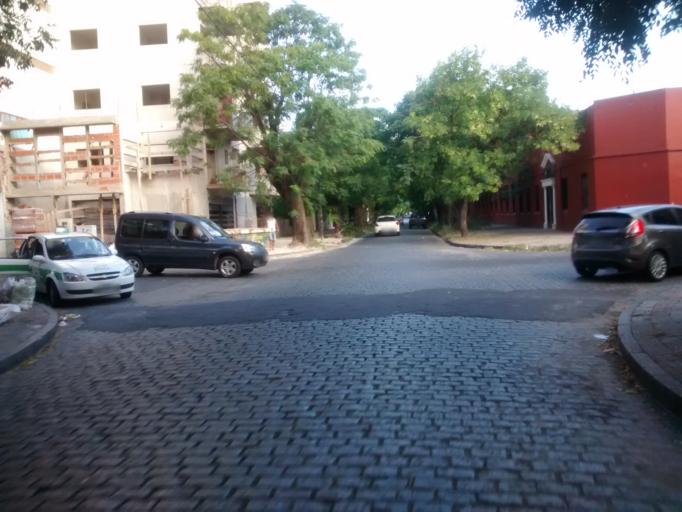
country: AR
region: Buenos Aires
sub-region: Partido de La Plata
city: La Plata
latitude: -34.9207
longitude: -57.9624
